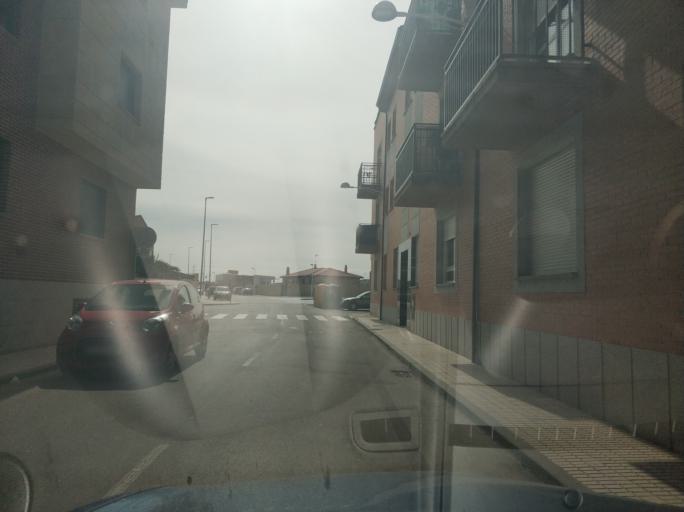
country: ES
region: Castille and Leon
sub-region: Provincia de Salamanca
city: Castellanos de Moriscos
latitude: 41.0174
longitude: -5.5915
